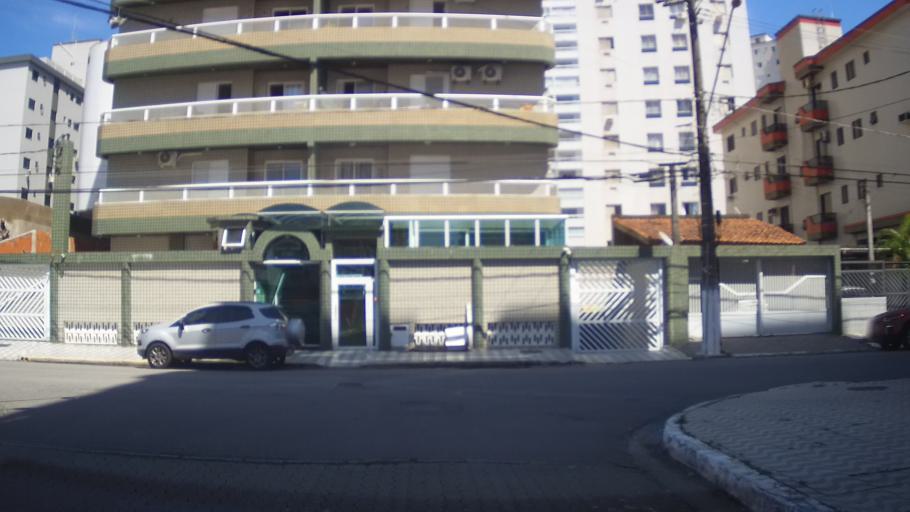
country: BR
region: Sao Paulo
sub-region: Praia Grande
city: Praia Grande
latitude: -24.0093
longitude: -46.4227
